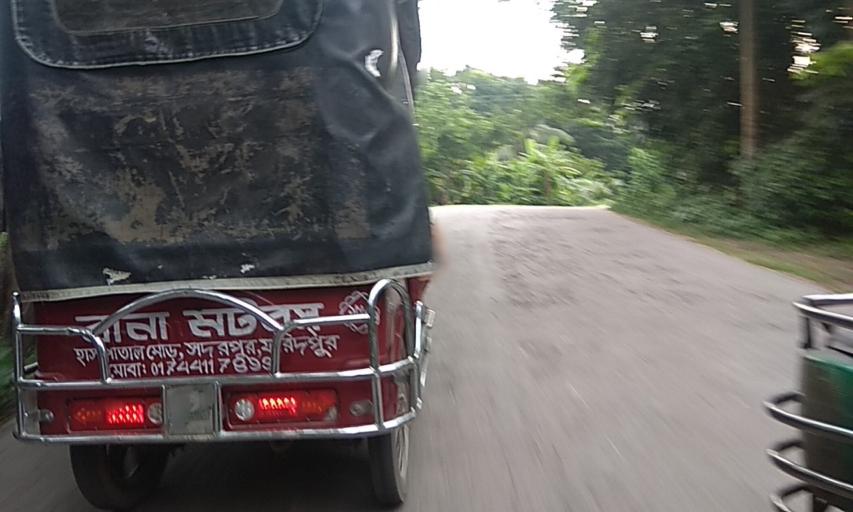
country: BD
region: Dhaka
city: Dohar
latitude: 23.4567
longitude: 90.0029
